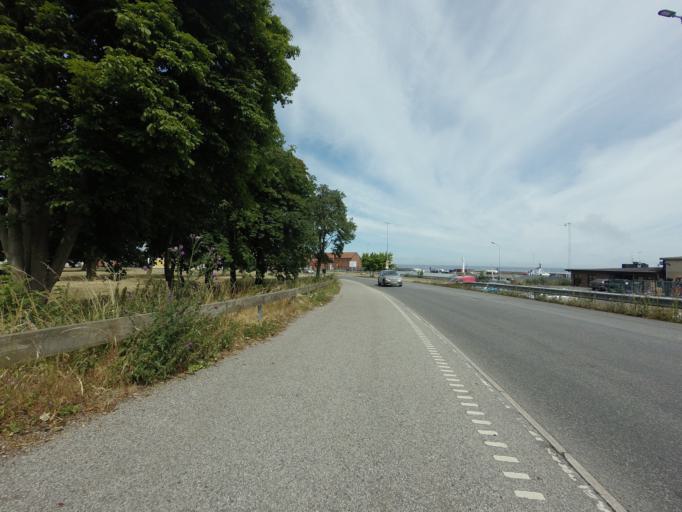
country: SE
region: Skane
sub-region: Simrishamns Kommun
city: Simrishamn
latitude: 55.5549
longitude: 14.3570
